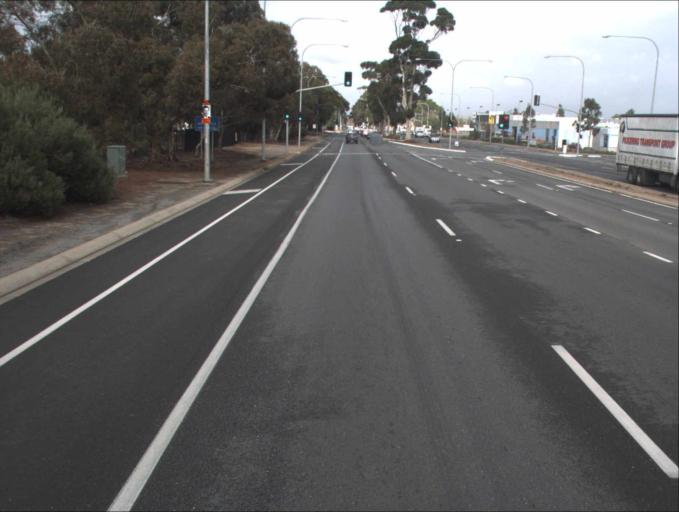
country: AU
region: South Australia
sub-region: Port Adelaide Enfield
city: Enfield
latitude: -34.8370
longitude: 138.6085
